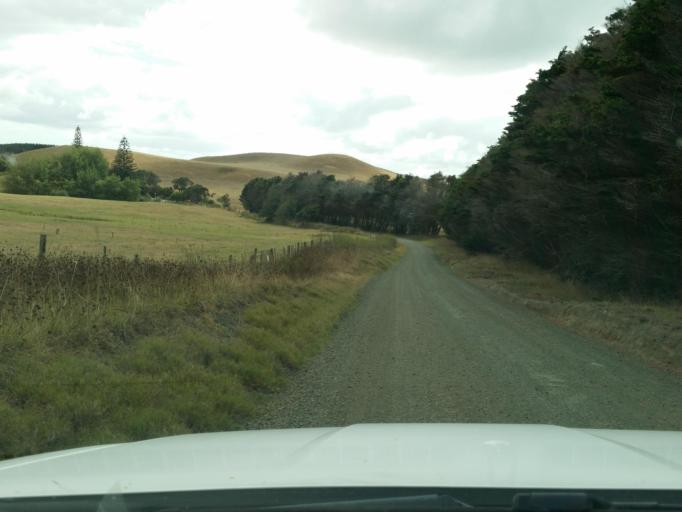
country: NZ
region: Auckland
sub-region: Auckland
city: Wellsford
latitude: -36.3443
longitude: 174.1683
